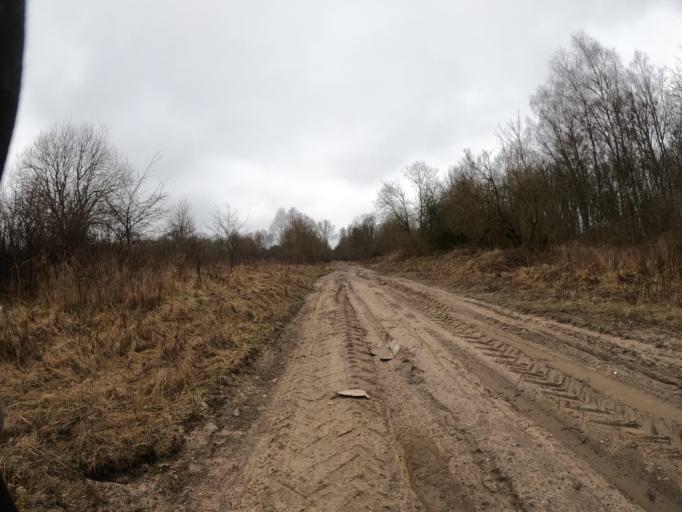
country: PL
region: Greater Poland Voivodeship
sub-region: Powiat zlotowski
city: Sypniewo
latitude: 53.4906
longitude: 16.5647
